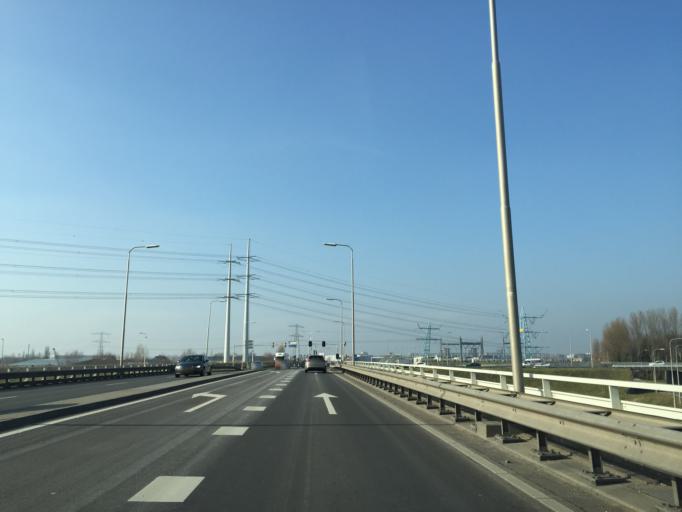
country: NL
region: South Holland
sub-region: Gemeente Rijswijk
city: Rijswijk
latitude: 52.0130
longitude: 4.3131
